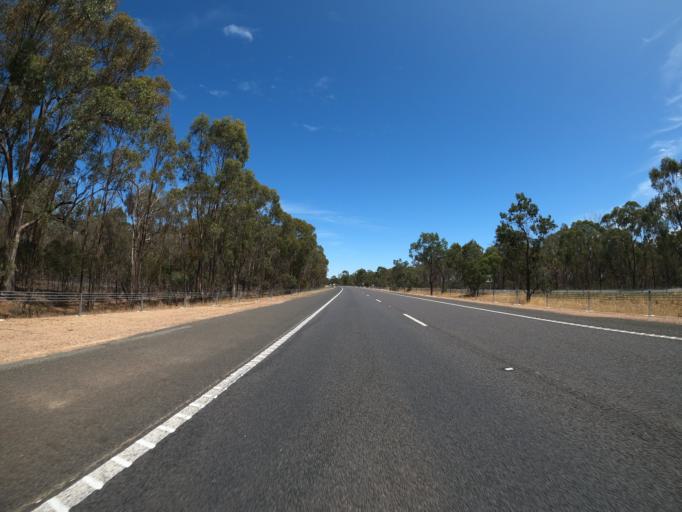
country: AU
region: Victoria
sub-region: Benalla
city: Benalla
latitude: -36.5786
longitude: 145.9426
